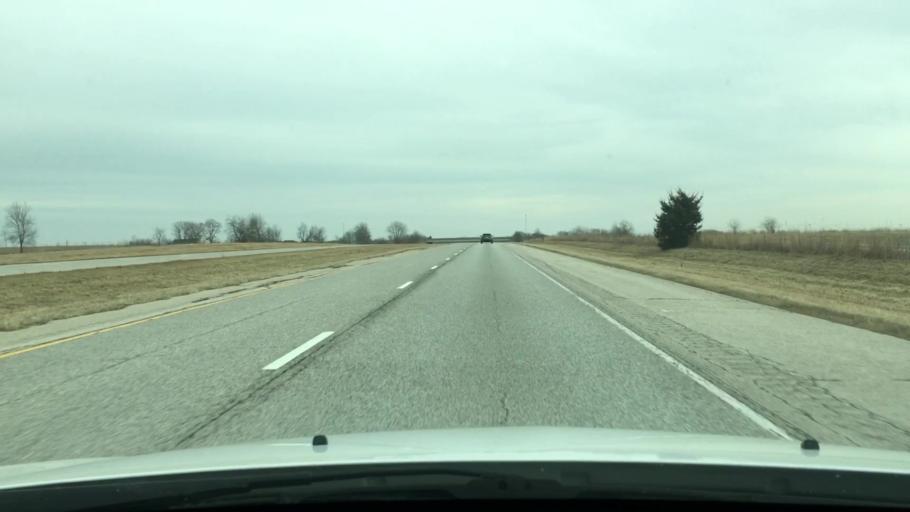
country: US
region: Illinois
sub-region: Pike County
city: Griggsville
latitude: 39.6782
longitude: -90.7113
